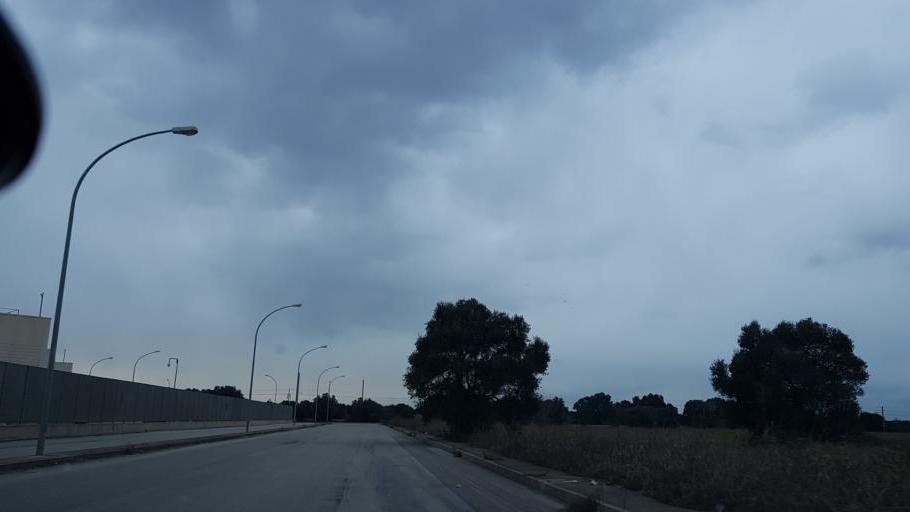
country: IT
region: Apulia
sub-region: Provincia di Brindisi
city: Mesagne
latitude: 40.5809
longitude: 17.8380
